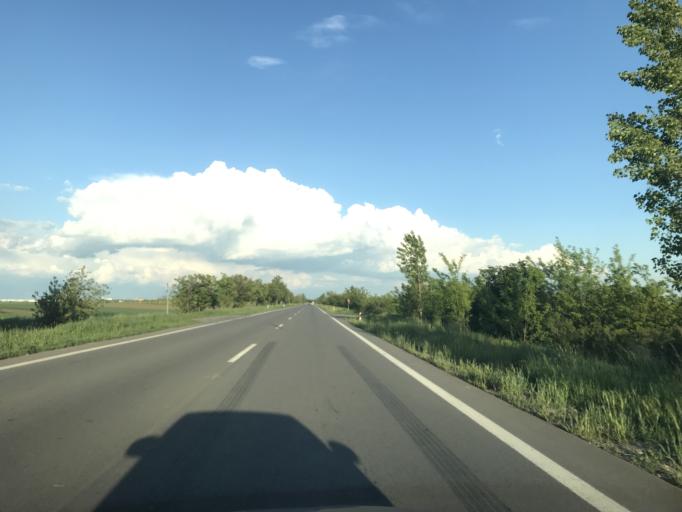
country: RS
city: Aradac
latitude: 45.3870
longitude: 20.3160
